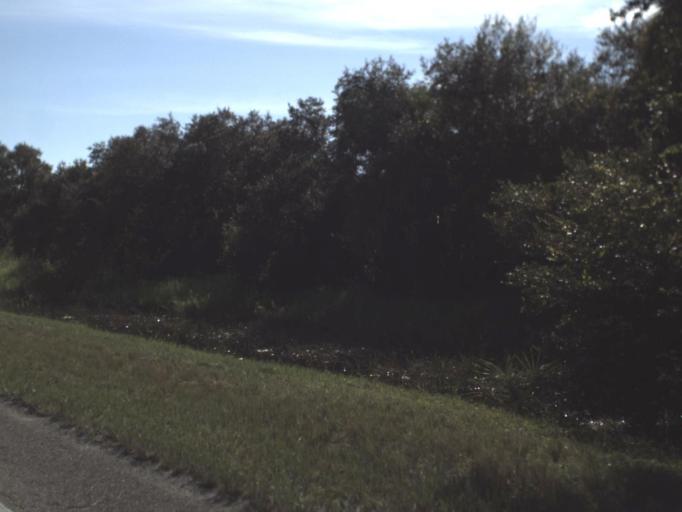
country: US
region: Florida
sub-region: Glades County
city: Moore Haven
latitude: 26.8961
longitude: -81.2383
